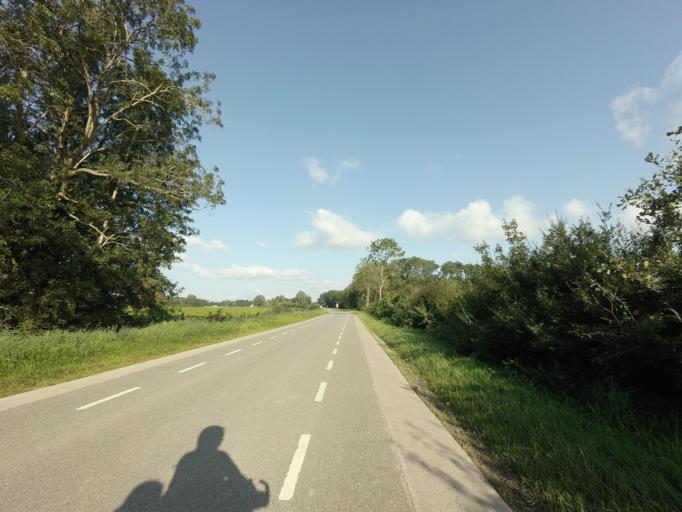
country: NL
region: Flevoland
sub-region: Gemeente Noordoostpolder
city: Ens
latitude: 52.6677
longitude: 5.7851
